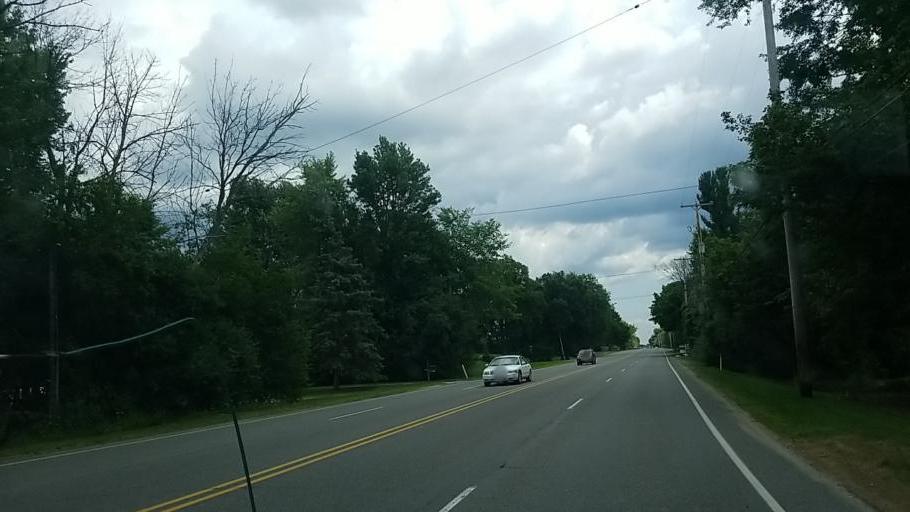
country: US
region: Michigan
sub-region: Kent County
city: East Grand Rapids
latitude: 42.9541
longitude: -85.5824
